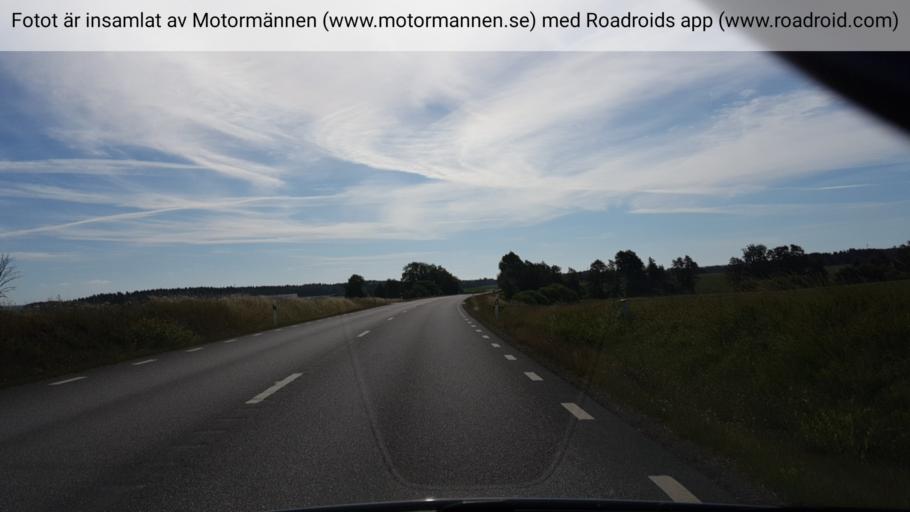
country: SE
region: Vaestra Goetaland
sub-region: Tibro Kommun
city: Tibro
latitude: 58.3517
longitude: 14.0806
